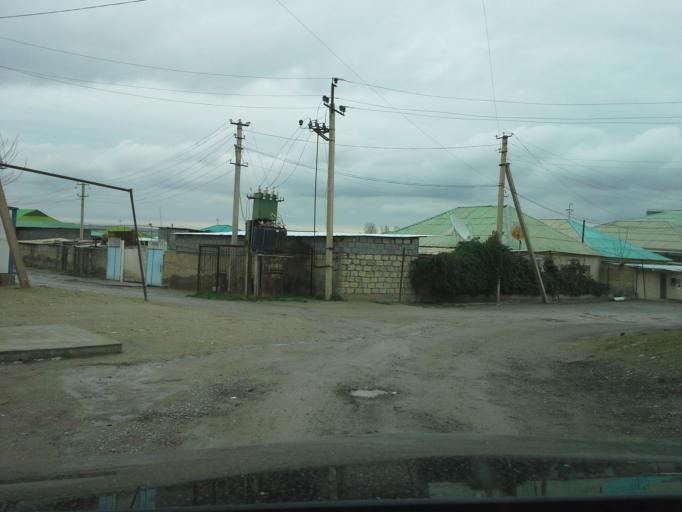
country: TM
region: Ahal
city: Abadan
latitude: 37.9594
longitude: 58.2191
